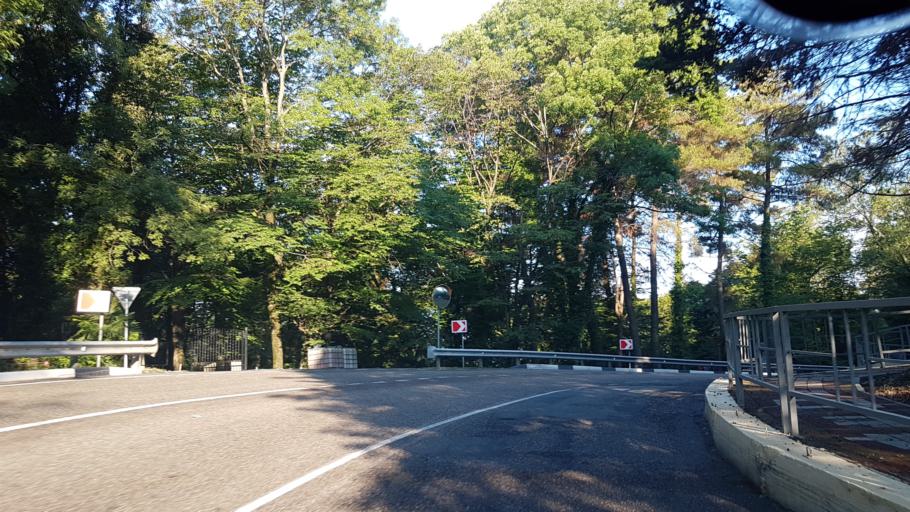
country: RU
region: Krasnodarskiy
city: Gornoye Loo
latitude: 43.6760
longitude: 39.6088
